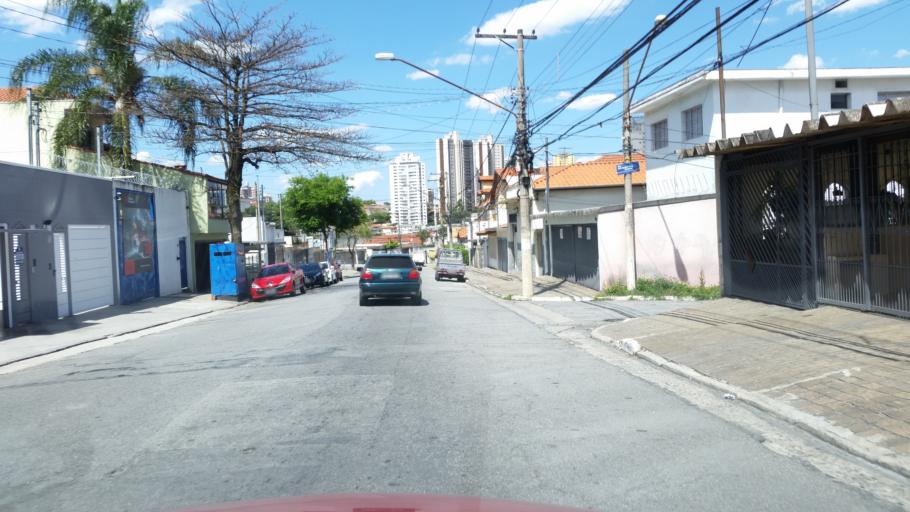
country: BR
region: Sao Paulo
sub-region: Diadema
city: Diadema
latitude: -23.6233
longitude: -46.6311
